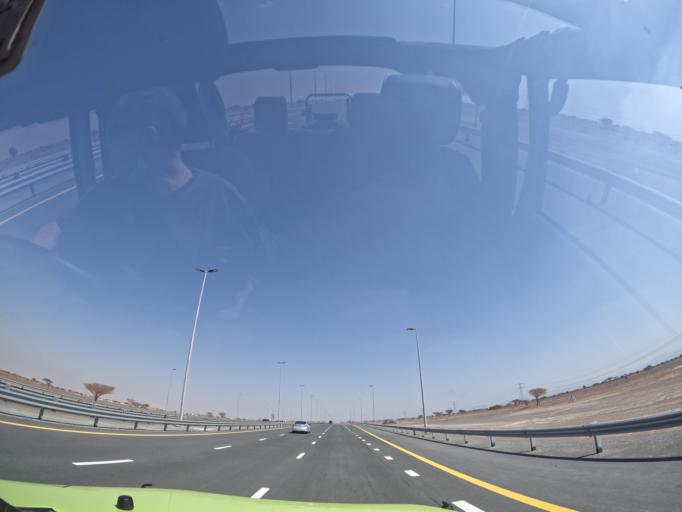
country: AE
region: Ash Shariqah
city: Adh Dhayd
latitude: 24.9520
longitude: 55.8351
